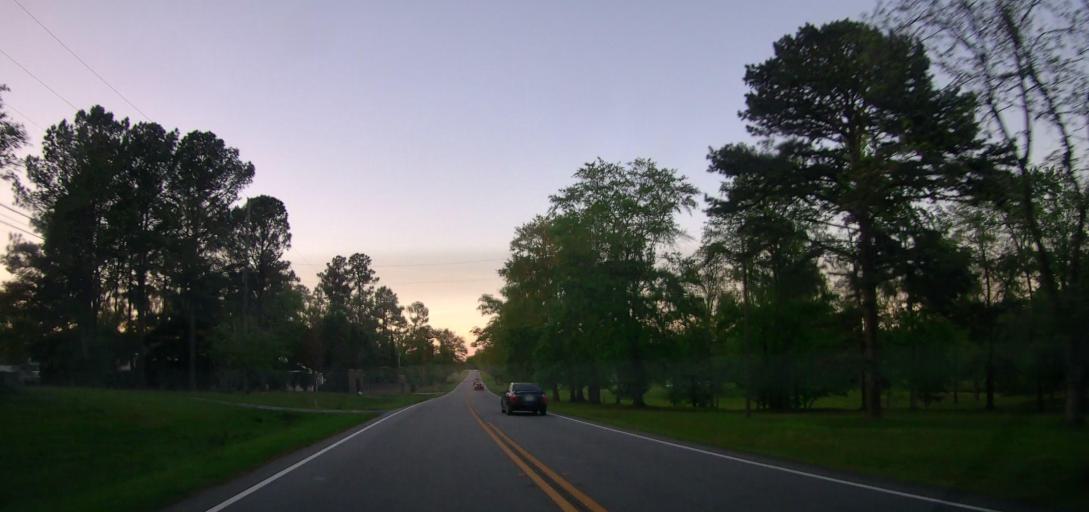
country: US
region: Georgia
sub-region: Marion County
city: Buena Vista
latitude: 32.3416
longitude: -84.5323
